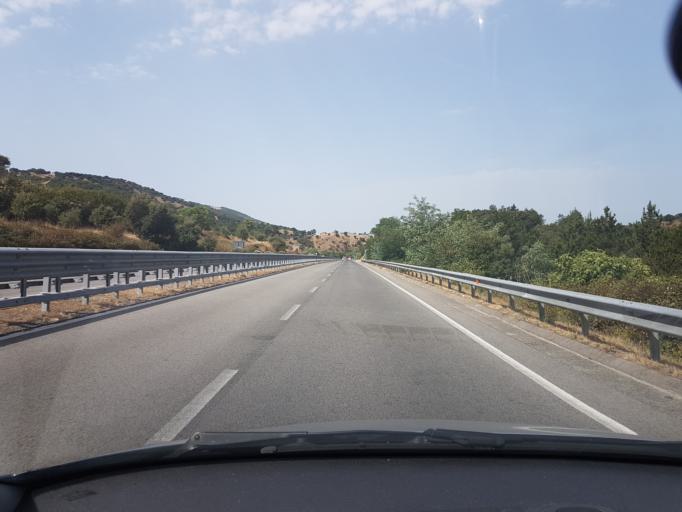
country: IT
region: Sardinia
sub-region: Provincia di Nuoro
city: Nuoro
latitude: 40.3149
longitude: 9.2472
